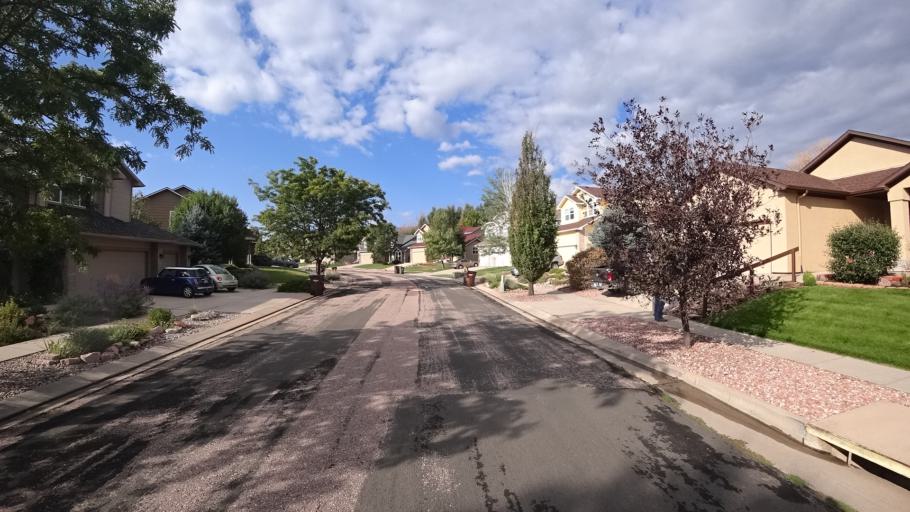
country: US
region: Colorado
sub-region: El Paso County
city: Manitou Springs
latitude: 38.9113
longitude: -104.8604
